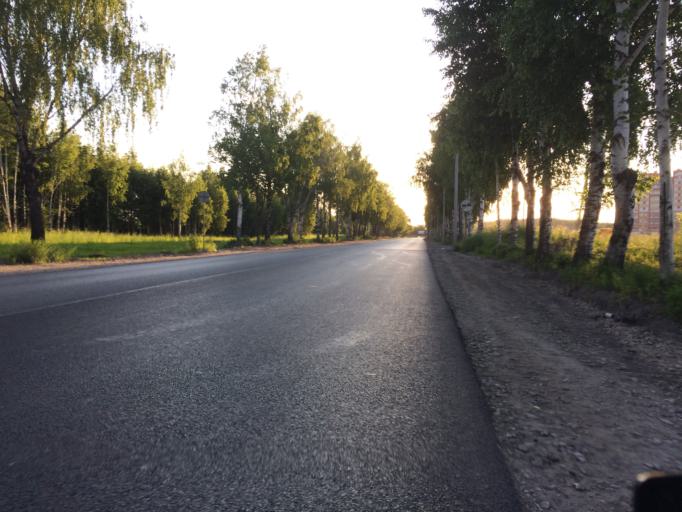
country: RU
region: Mariy-El
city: Medvedevo
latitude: 56.6502
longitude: 47.8323
